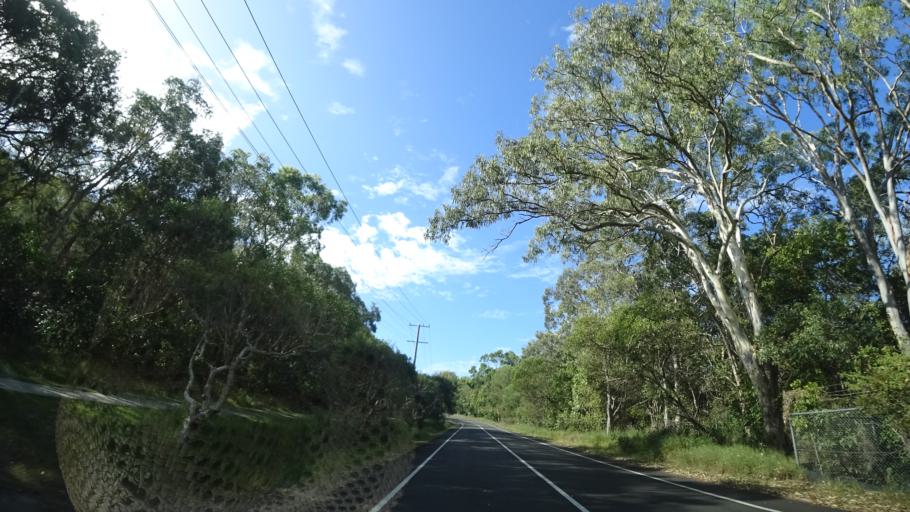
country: AU
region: Queensland
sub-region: Sunshine Coast
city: Coolum Beach
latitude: -26.5607
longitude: 153.0908
